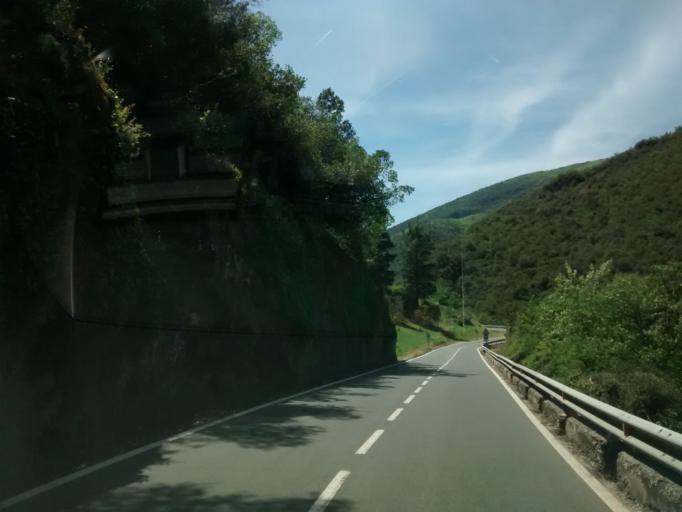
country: ES
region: Cantabria
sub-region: Provincia de Cantabria
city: Potes
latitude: 43.1169
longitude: -4.6323
